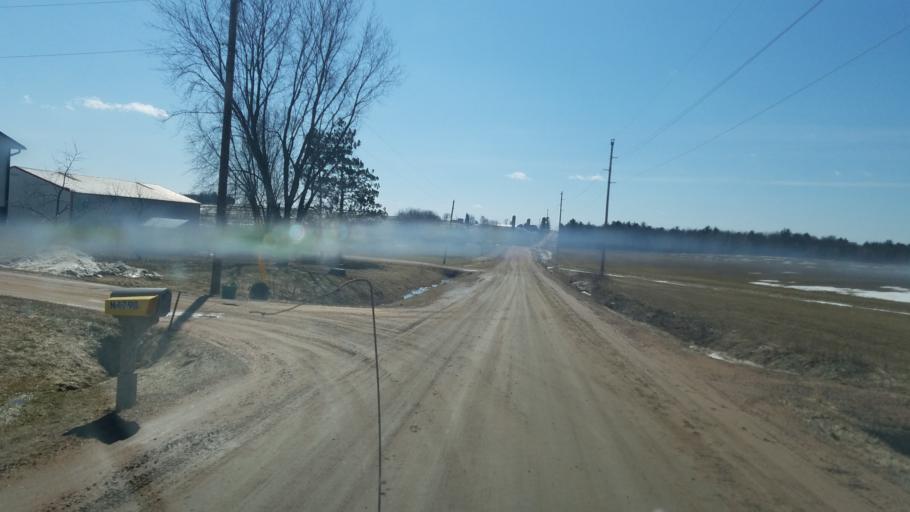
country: US
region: Wisconsin
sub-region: Clark County
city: Loyal
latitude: 44.5934
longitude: -90.3962
